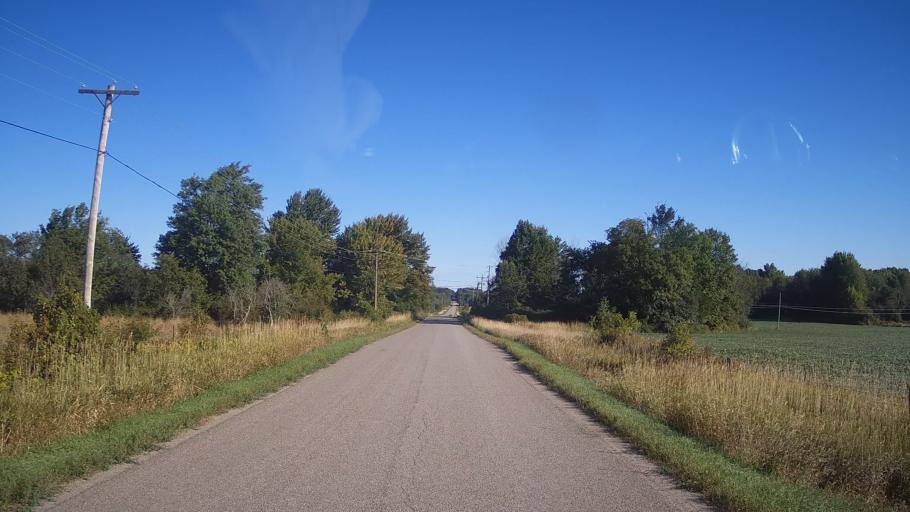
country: US
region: New York
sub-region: Jefferson County
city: Alexandria Bay
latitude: 44.4306
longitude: -75.9807
